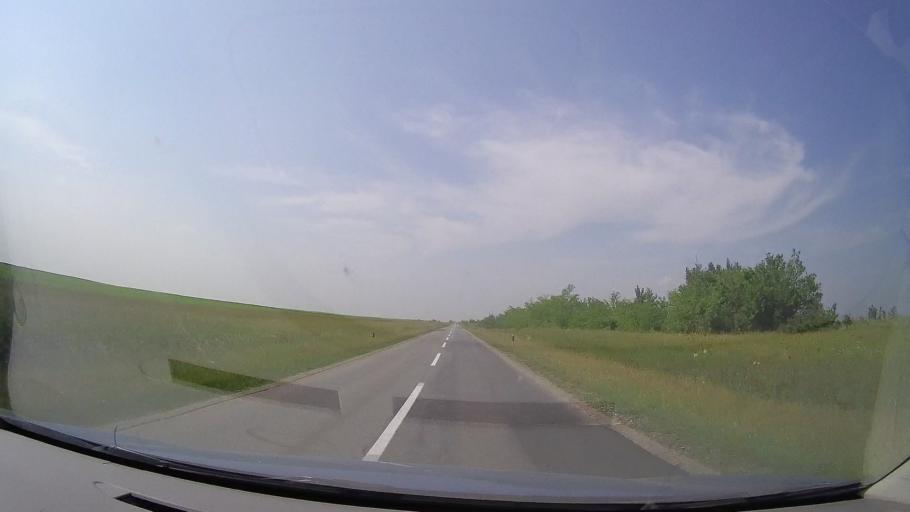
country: RS
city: Samos
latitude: 45.1872
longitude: 20.7643
